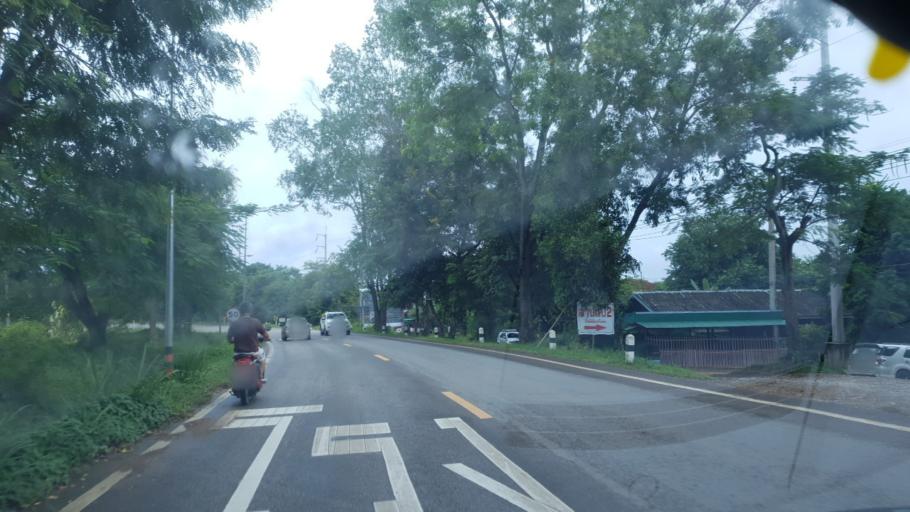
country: TH
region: Mae Hong Son
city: Ban Huai I Huak
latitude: 18.1705
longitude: 97.9336
